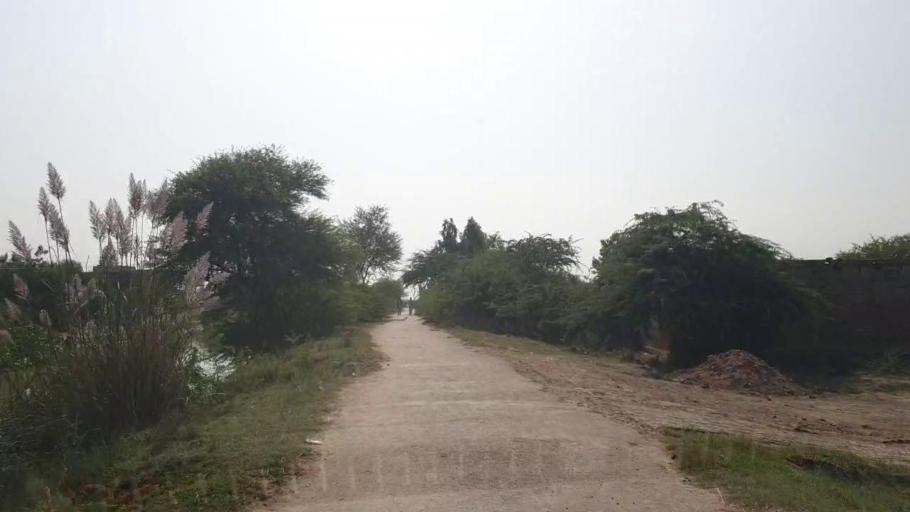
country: PK
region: Sindh
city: Badin
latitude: 24.6400
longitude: 68.8492
